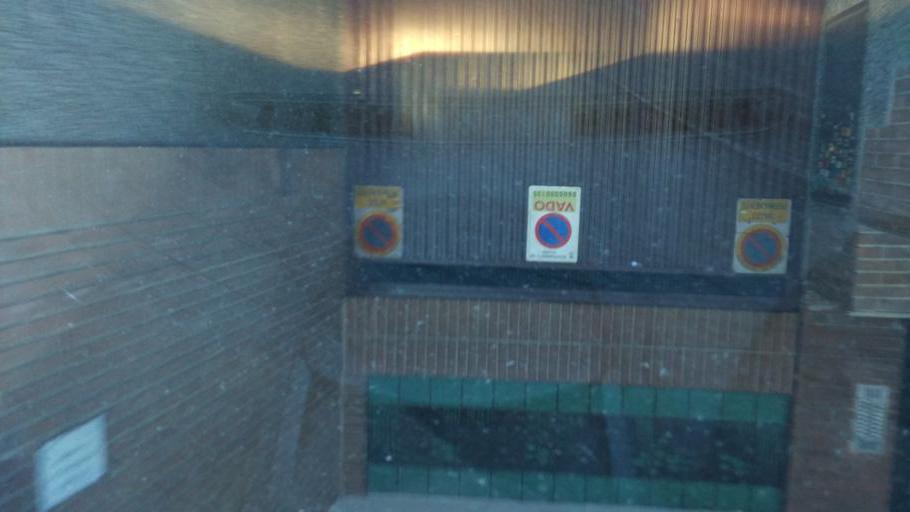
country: ES
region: Madrid
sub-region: Provincia de Madrid
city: Tetuan de las Victorias
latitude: 40.4697
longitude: -3.7023
